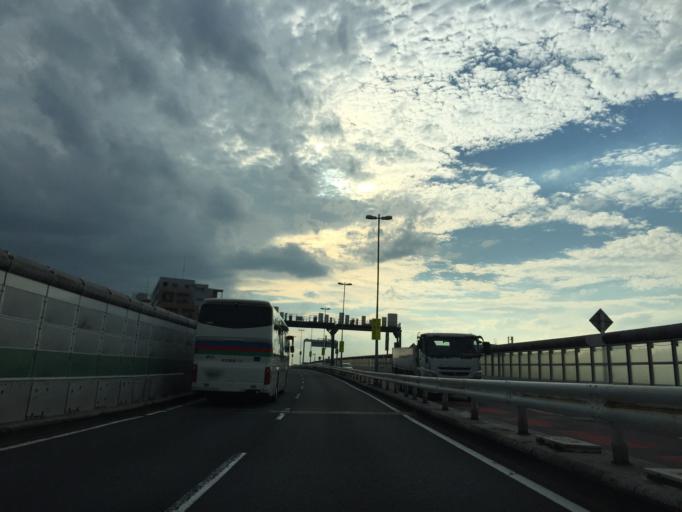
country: JP
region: Tokyo
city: Chofugaoka
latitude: 35.6268
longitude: 139.6294
